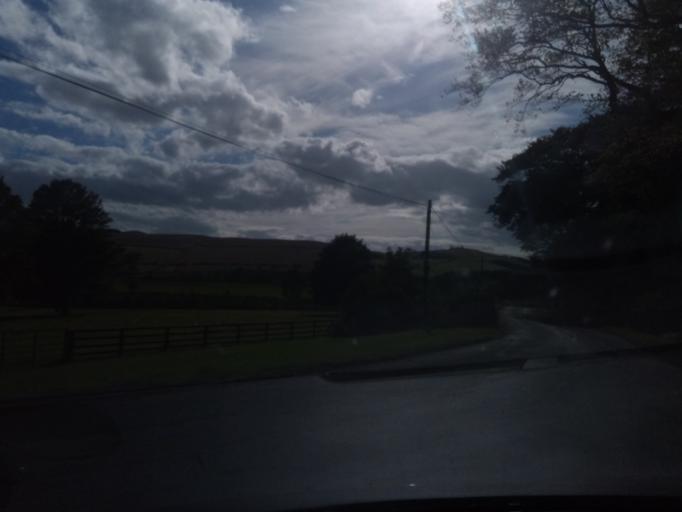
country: GB
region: England
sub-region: Northumberland
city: Kirknewton
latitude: 55.5939
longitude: -2.1857
